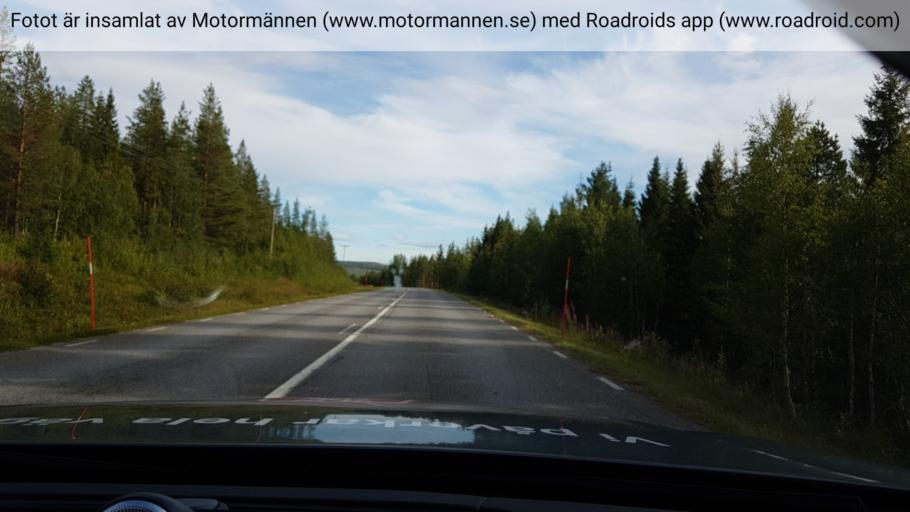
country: SE
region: Jaemtland
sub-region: Stroemsunds Kommun
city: Stroemsund
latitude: 64.2614
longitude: 15.3980
